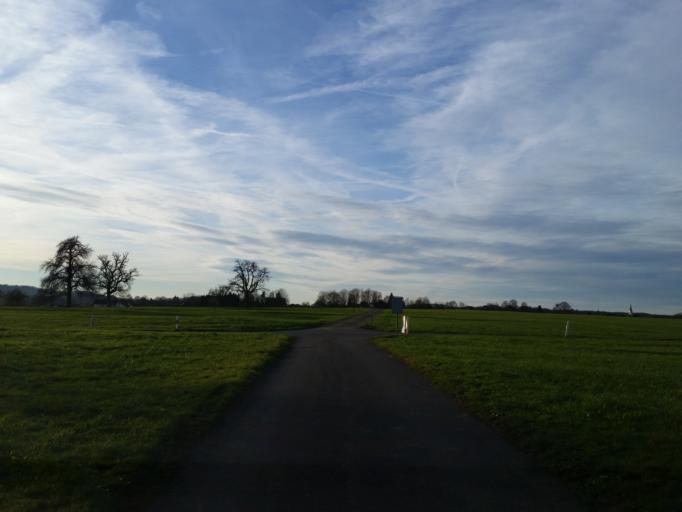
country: CH
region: Thurgau
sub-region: Arbon District
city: Amriswil
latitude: 47.5578
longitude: 9.3188
